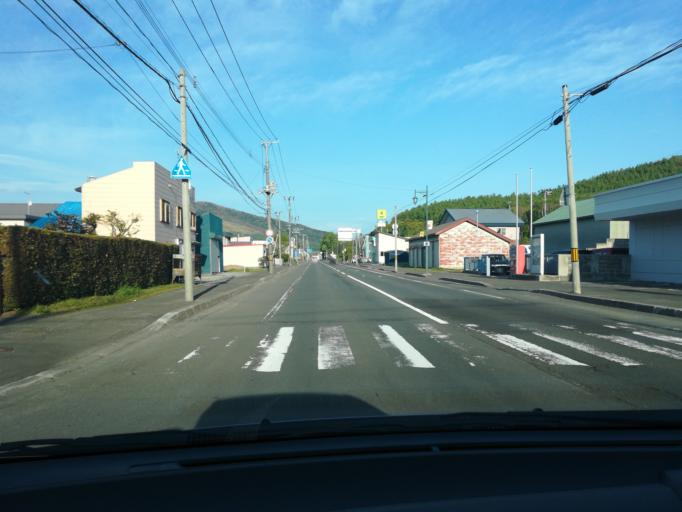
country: JP
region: Hokkaido
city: Shimo-furano
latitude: 43.1628
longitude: 142.5706
